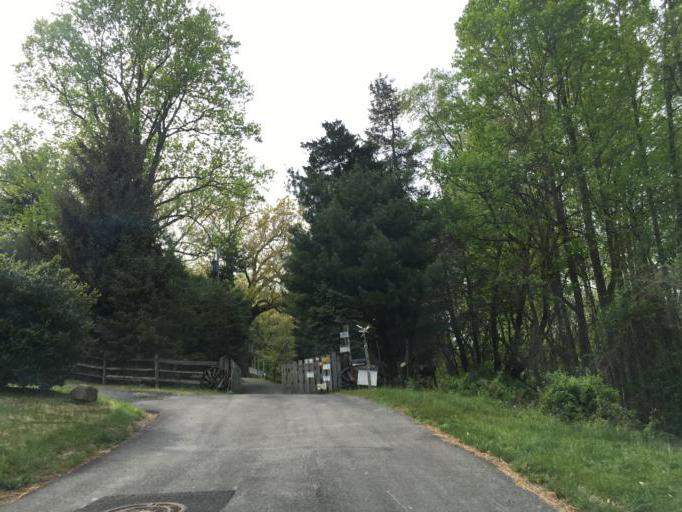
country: US
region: Maryland
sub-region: Howard County
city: Elkridge
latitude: 39.2250
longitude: -76.7253
